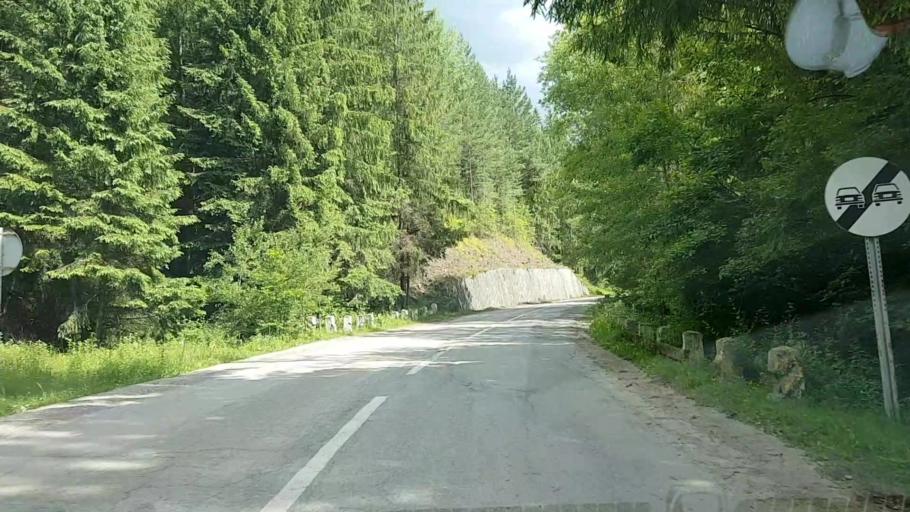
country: RO
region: Neamt
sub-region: Comuna Hangu
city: Hangu
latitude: 47.0525
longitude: 26.0053
